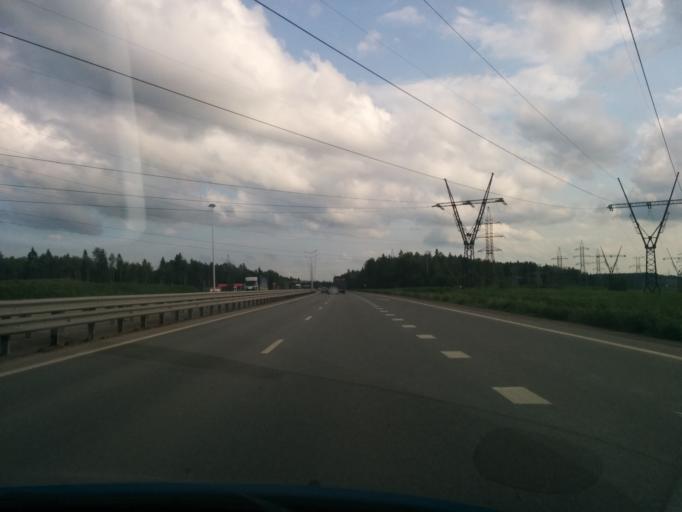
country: RU
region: Perm
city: Novyye Lyady
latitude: 58.0441
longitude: 56.4305
